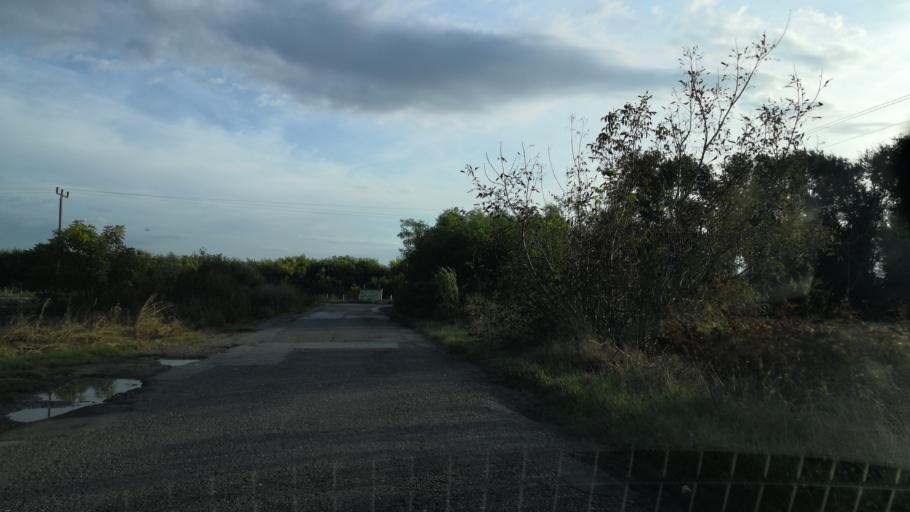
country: RS
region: Autonomna Pokrajina Vojvodina
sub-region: Sremski Okrug
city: Stara Pazova
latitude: 44.9974
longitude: 20.1642
